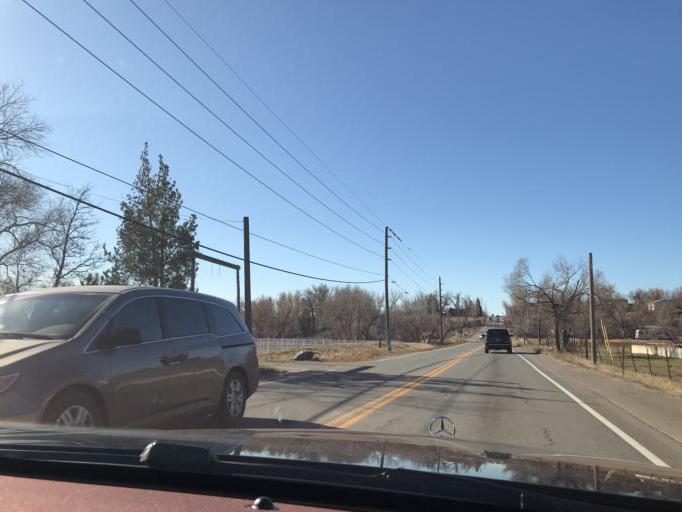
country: US
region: Colorado
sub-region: Jefferson County
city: Applewood
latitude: 39.8406
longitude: -105.1653
